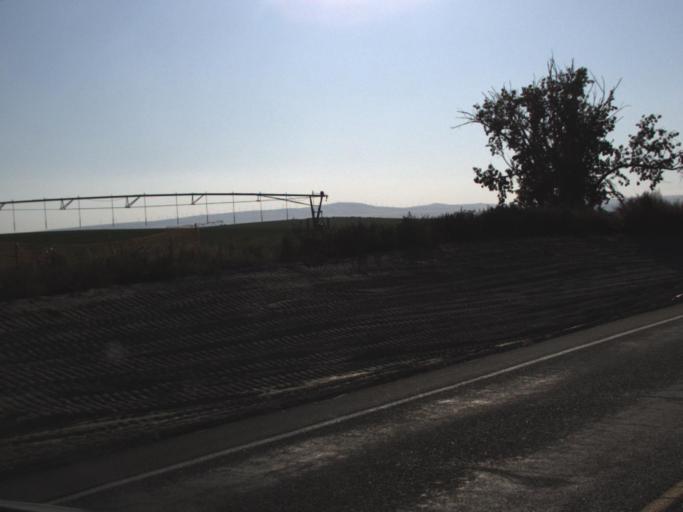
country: US
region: Washington
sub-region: Walla Walla County
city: Burbank
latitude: 46.2152
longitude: -118.9119
